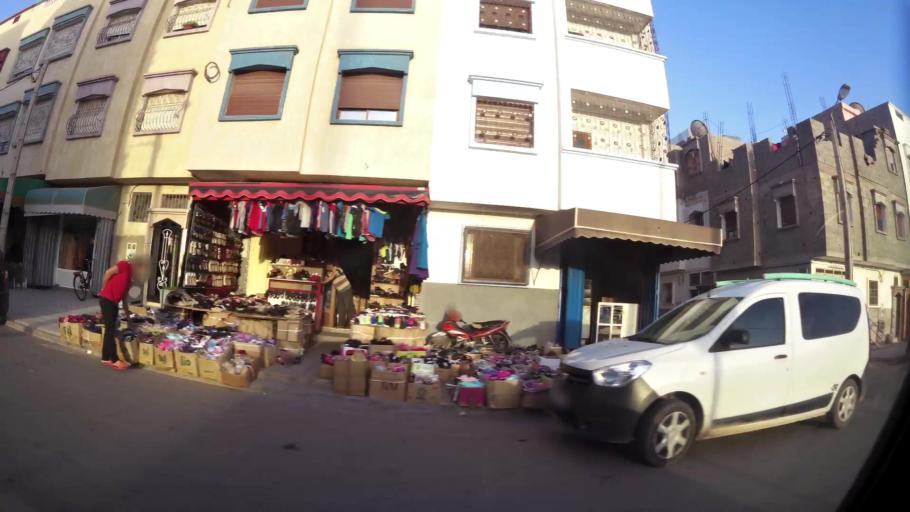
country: MA
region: Oued ed Dahab-Lagouira
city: Dakhla
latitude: 30.3973
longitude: -9.5618
